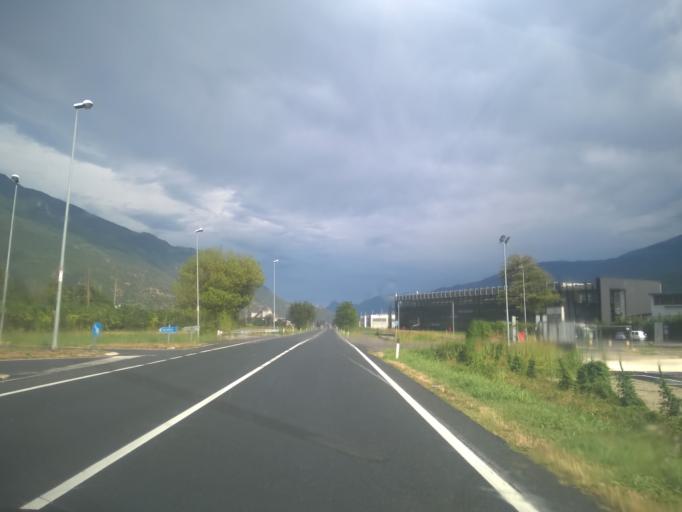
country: IT
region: Piedmont
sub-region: Provincia di Torino
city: Bruzolo
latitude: 45.1332
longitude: 7.1882
